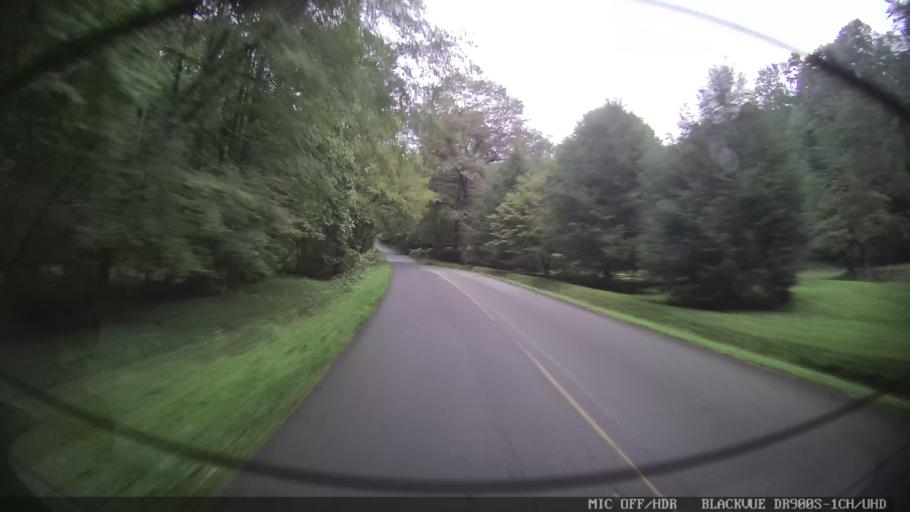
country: US
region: Georgia
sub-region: Gilmer County
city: Ellijay
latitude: 34.7561
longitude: -84.5291
